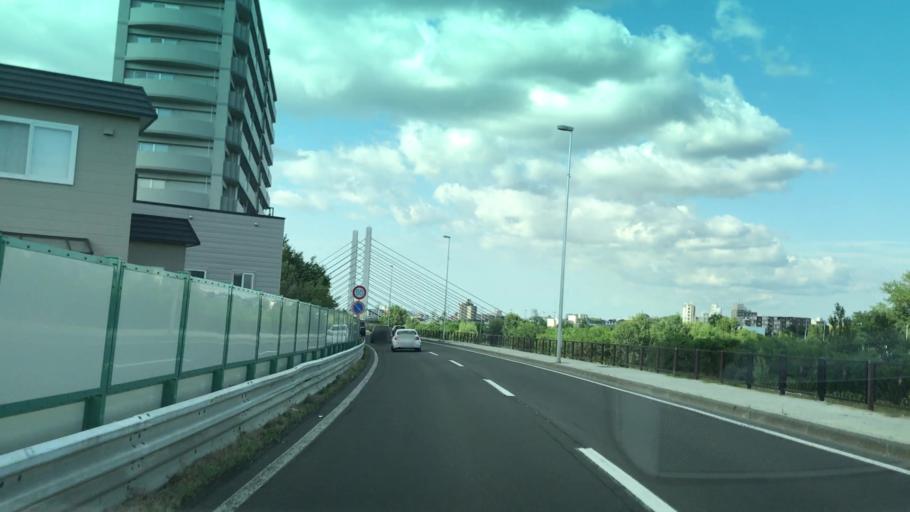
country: JP
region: Hokkaido
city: Sapporo
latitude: 43.0129
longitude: 141.3514
